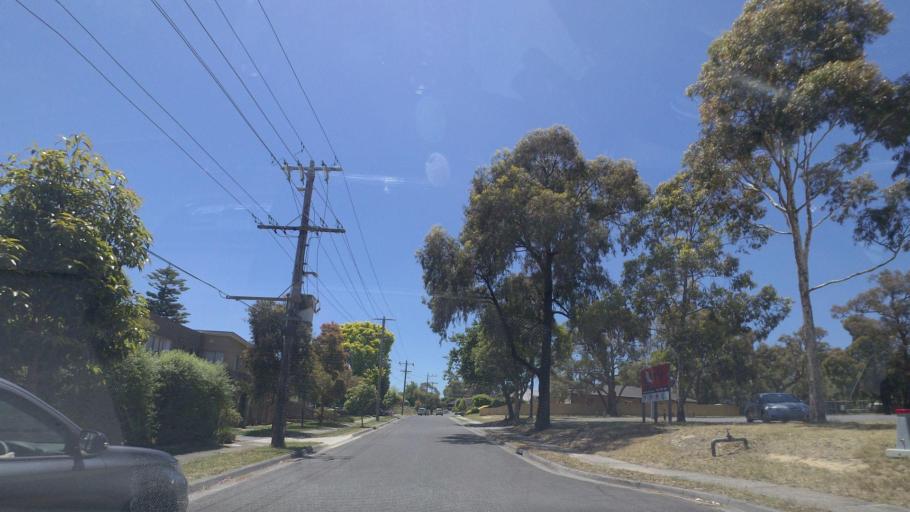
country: AU
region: Victoria
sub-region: Knox
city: Boronia
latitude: -37.8810
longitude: 145.2758
